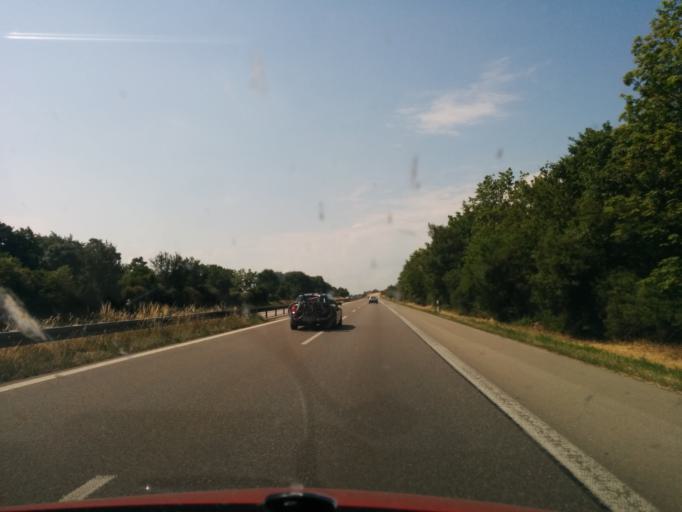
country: DE
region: Bavaria
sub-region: Swabia
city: Kleinaitingen
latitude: 48.1968
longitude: 10.8518
